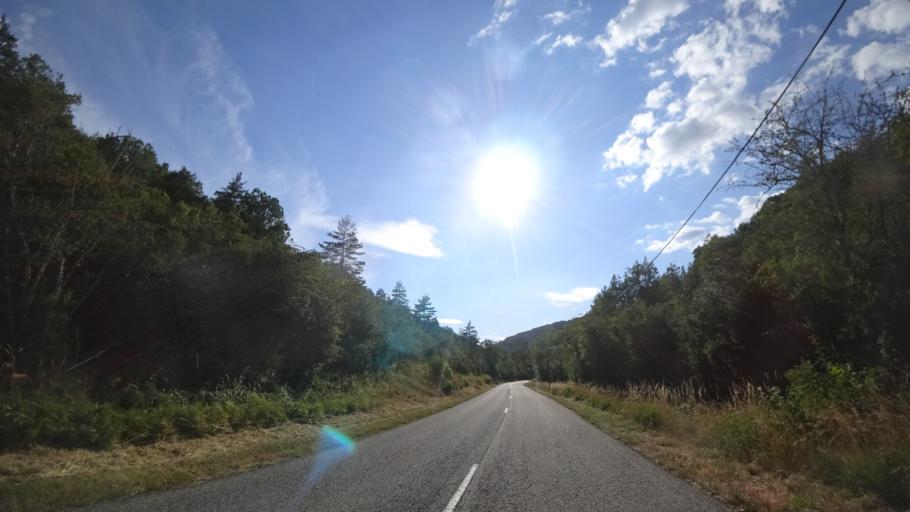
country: FR
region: Languedoc-Roussillon
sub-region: Departement de la Lozere
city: La Canourgue
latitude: 44.4107
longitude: 3.2706
